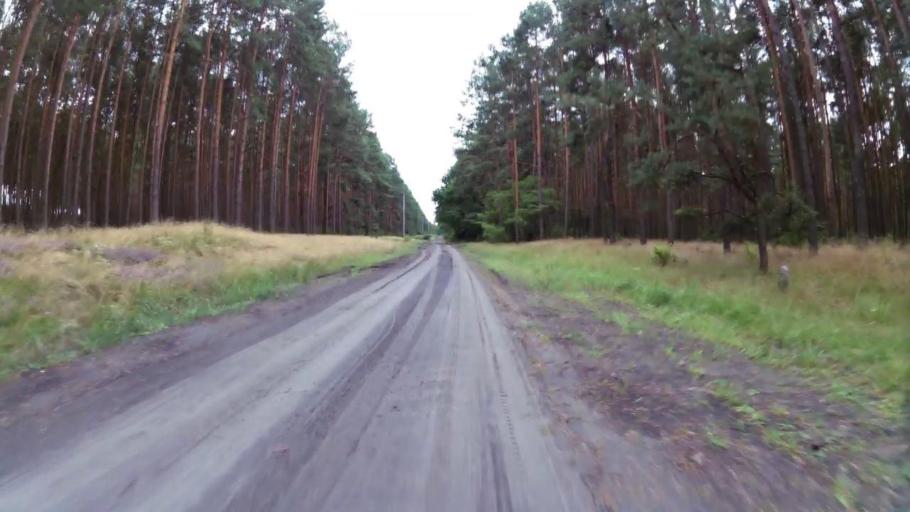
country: PL
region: West Pomeranian Voivodeship
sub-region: Powiat mysliborski
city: Debno
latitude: 52.8076
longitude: 14.7209
